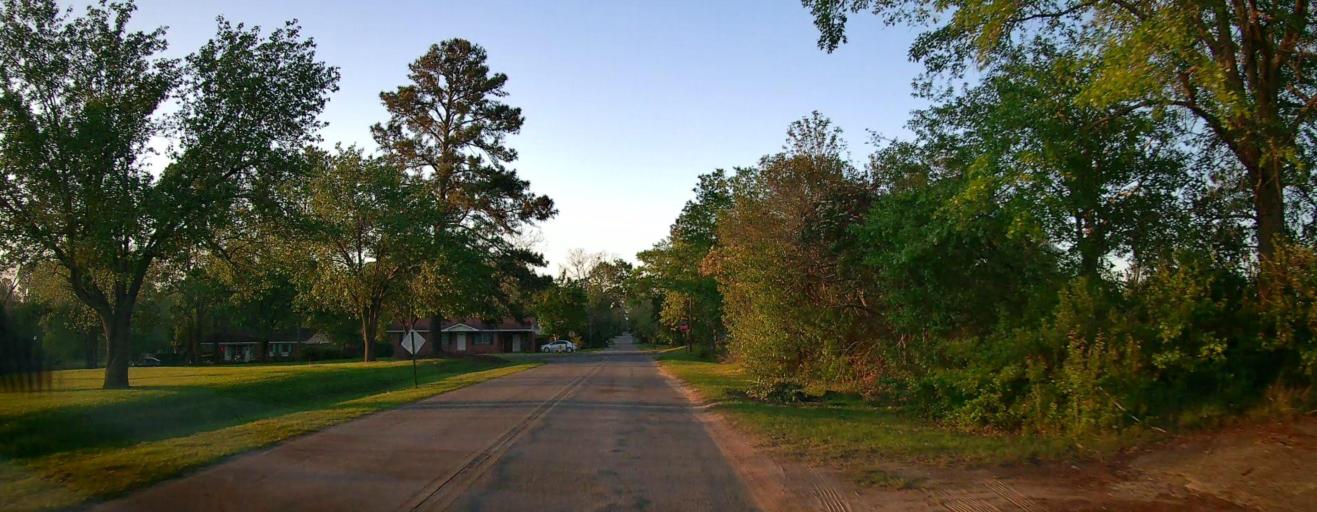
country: US
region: Georgia
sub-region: Ben Hill County
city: Fitzgerald
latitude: 31.7106
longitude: -83.2623
